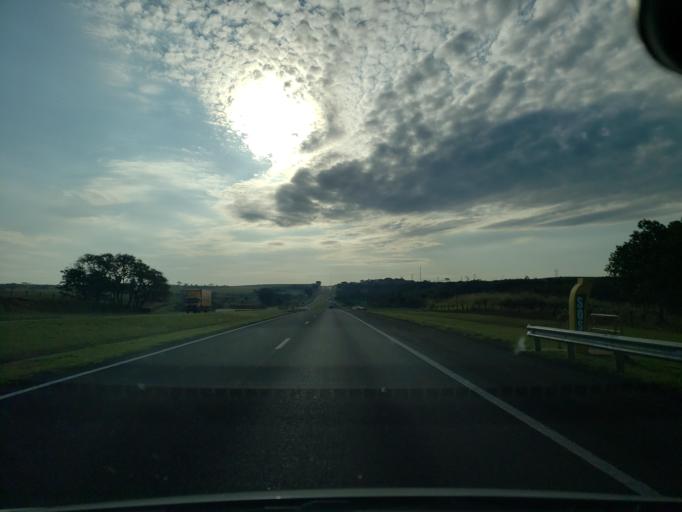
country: BR
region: Sao Paulo
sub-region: Valparaiso
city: Valparaiso
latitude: -21.1697
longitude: -50.9346
